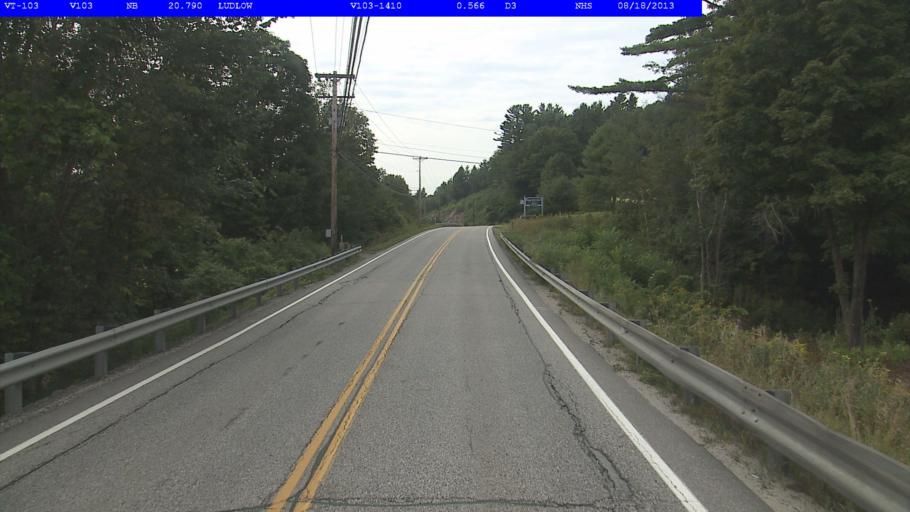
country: US
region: Vermont
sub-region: Windsor County
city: Chester
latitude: 43.3899
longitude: -72.6724
